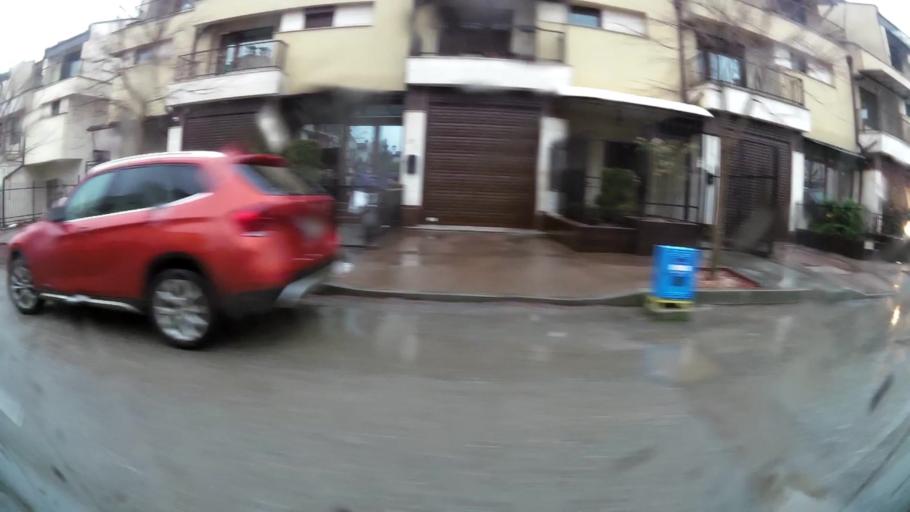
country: BG
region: Sofia-Capital
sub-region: Stolichna Obshtina
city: Sofia
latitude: 42.6494
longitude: 23.3193
